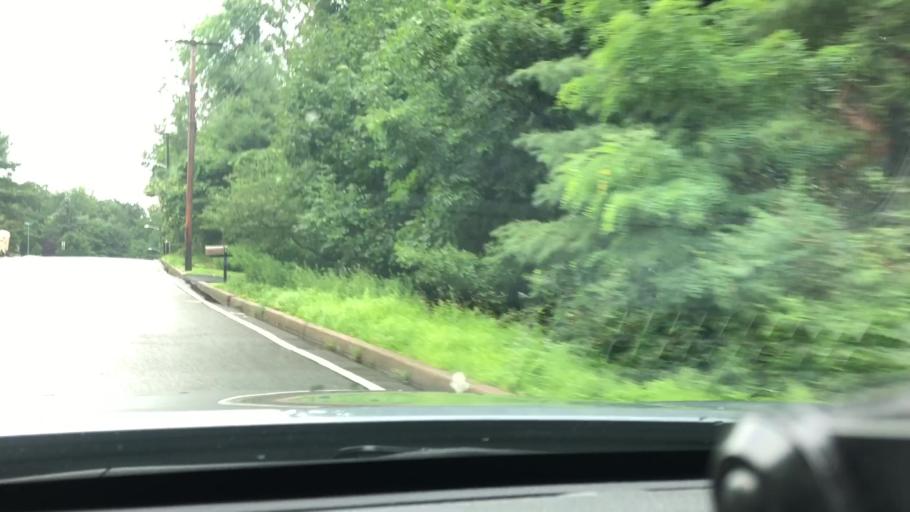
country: US
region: New Jersey
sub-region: Bergen County
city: Waldwick
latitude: 41.0131
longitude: -74.1050
